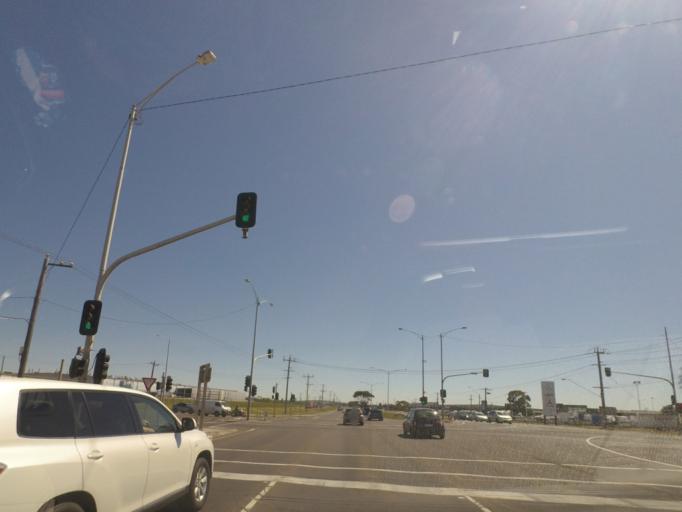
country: AU
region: Victoria
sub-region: Hume
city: Coolaroo
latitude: -37.6436
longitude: 144.9512
